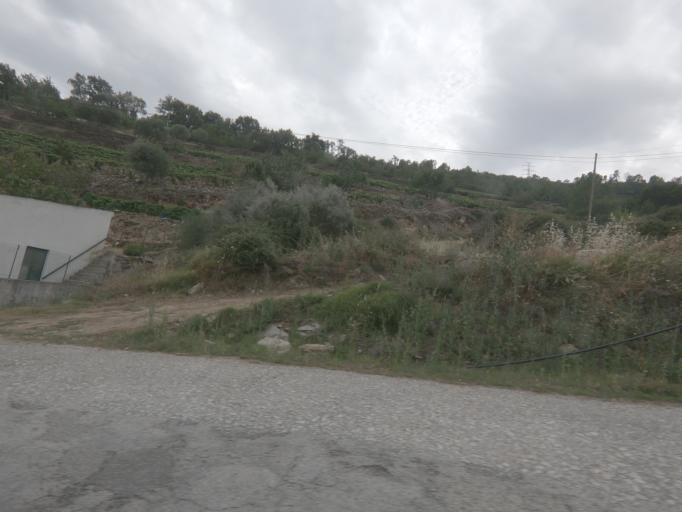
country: PT
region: Viseu
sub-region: Armamar
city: Armamar
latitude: 41.1259
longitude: -7.6402
